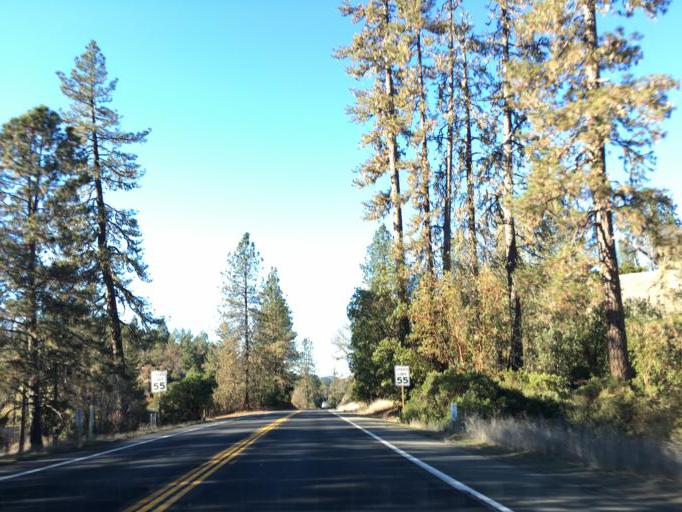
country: US
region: California
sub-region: Mendocino County
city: Laytonville
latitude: 39.7320
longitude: -123.5106
